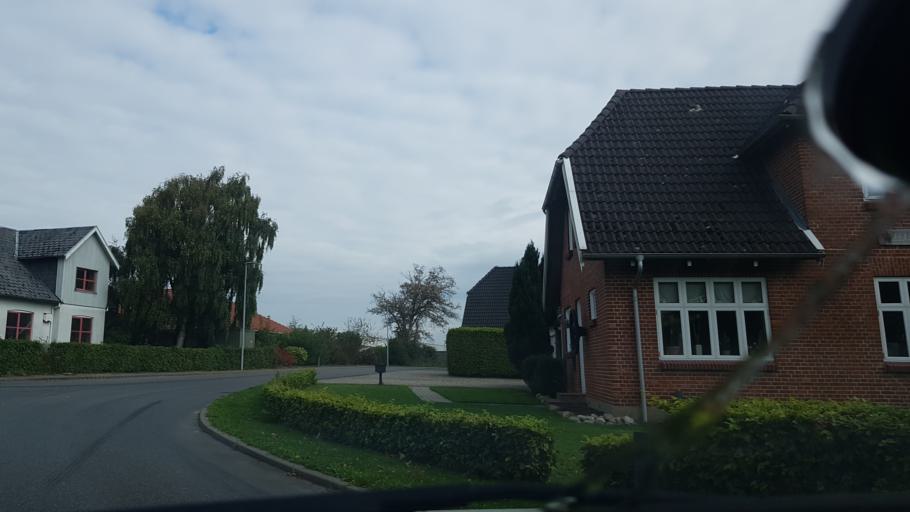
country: DK
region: South Denmark
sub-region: Vejen Kommune
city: Holsted
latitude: 55.4517
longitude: 8.9383
